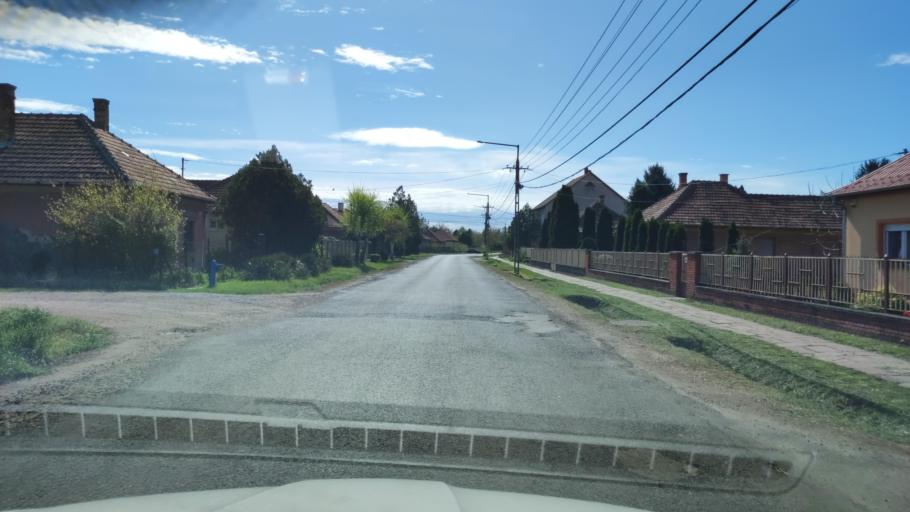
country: HU
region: Pest
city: Abony
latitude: 47.1812
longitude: 20.0092
